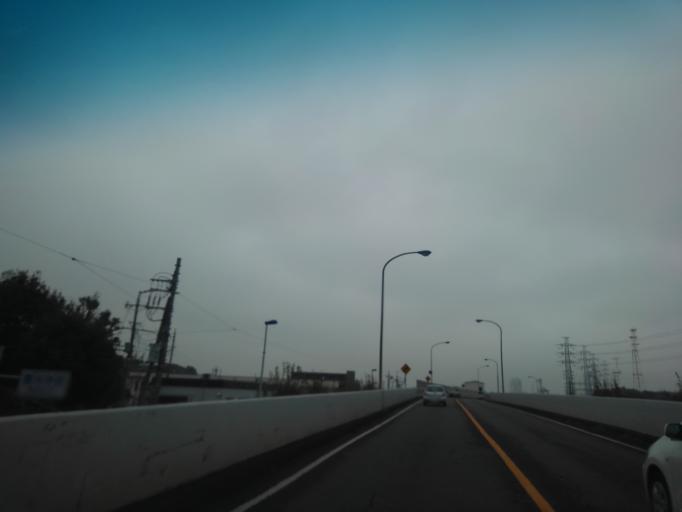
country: JP
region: Tokyo
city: Hachioji
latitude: 35.6813
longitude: 139.3523
